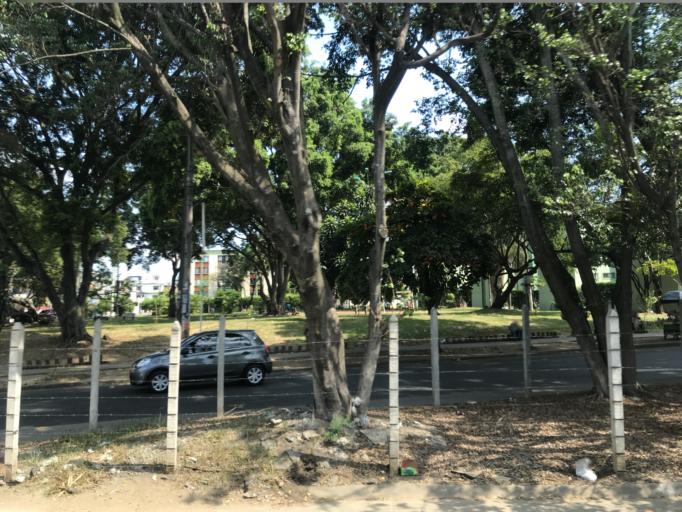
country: CO
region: Valle del Cauca
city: Cali
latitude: 3.4889
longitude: -76.4983
